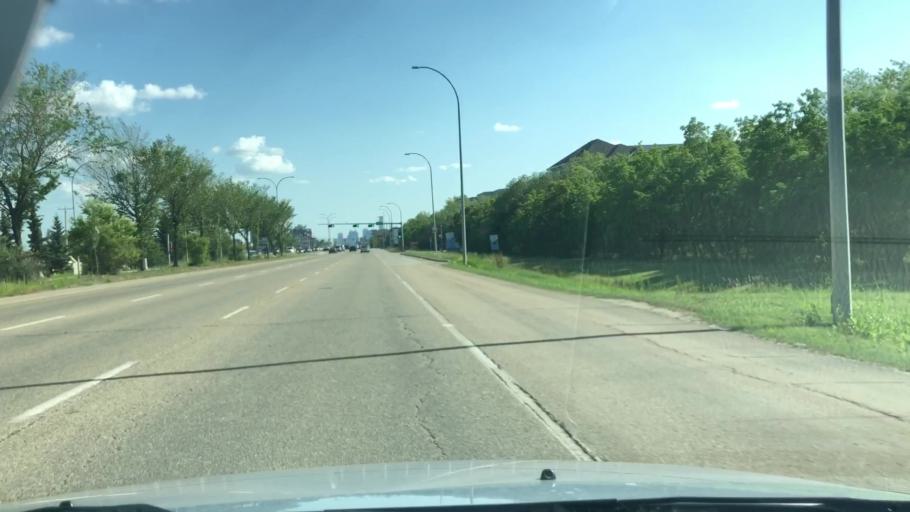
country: CA
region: Alberta
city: Edmonton
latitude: 53.6040
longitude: -113.4921
